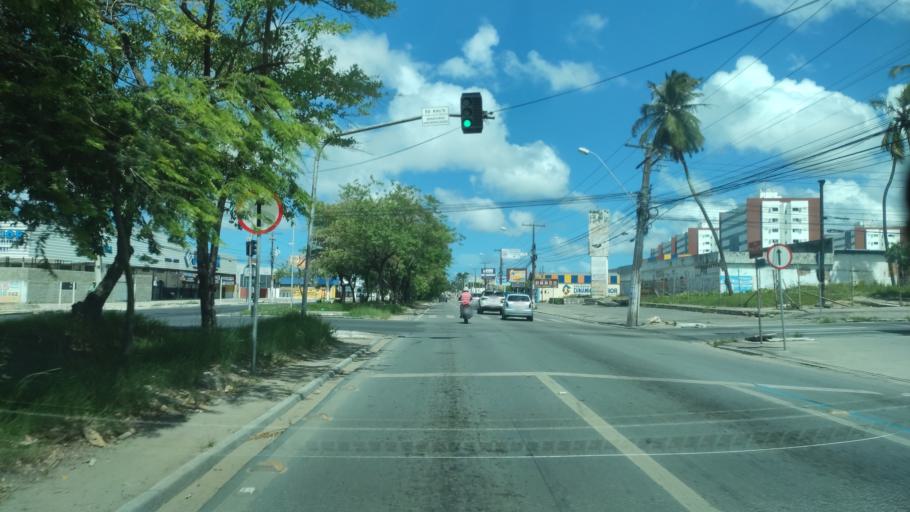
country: BR
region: Alagoas
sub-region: Satuba
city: Satuba
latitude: -9.5771
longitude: -35.7701
